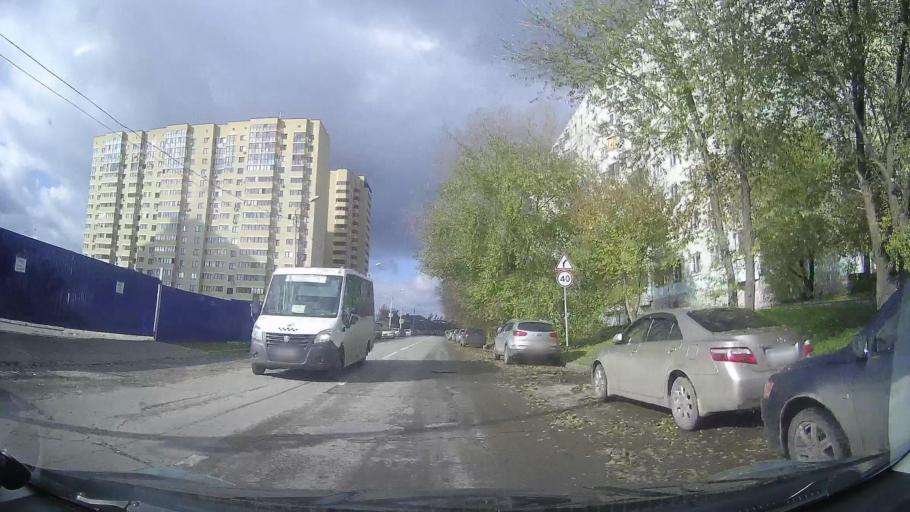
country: RU
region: Rostov
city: Severnyy
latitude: 47.2908
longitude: 39.6883
